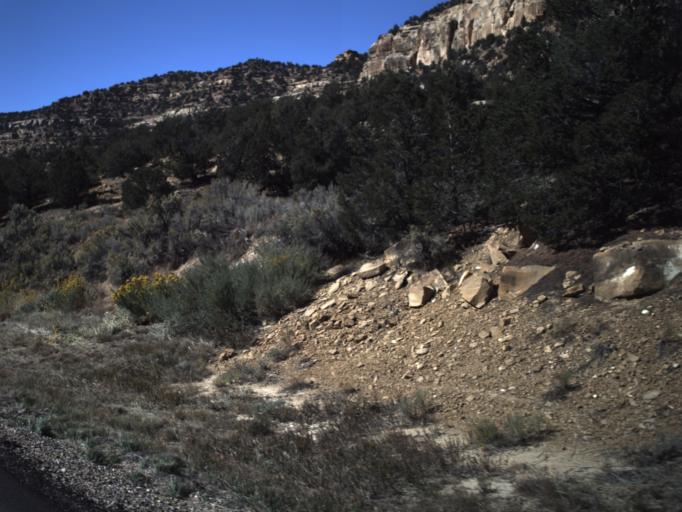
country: US
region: Utah
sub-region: Wayne County
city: Loa
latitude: 37.7402
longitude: -111.7128
